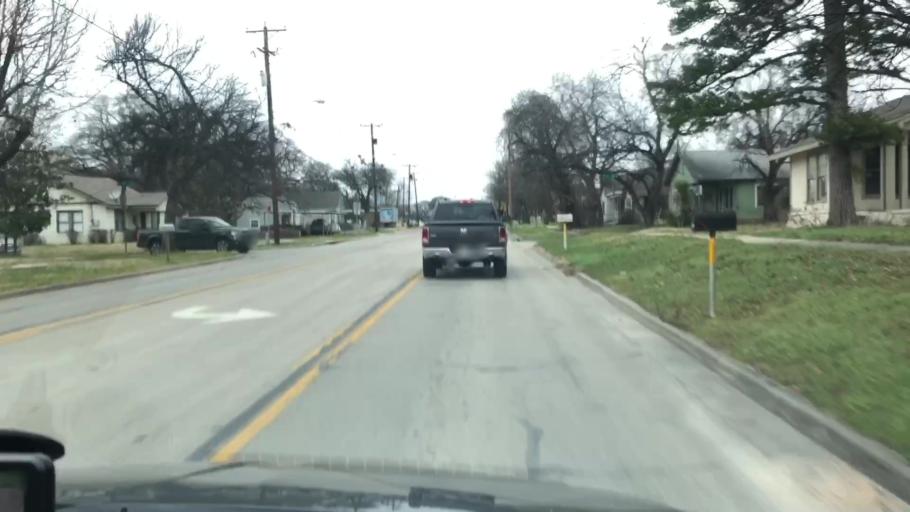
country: US
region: Texas
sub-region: Palo Pinto County
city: Mineral Wells
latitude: 32.8225
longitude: -98.1128
